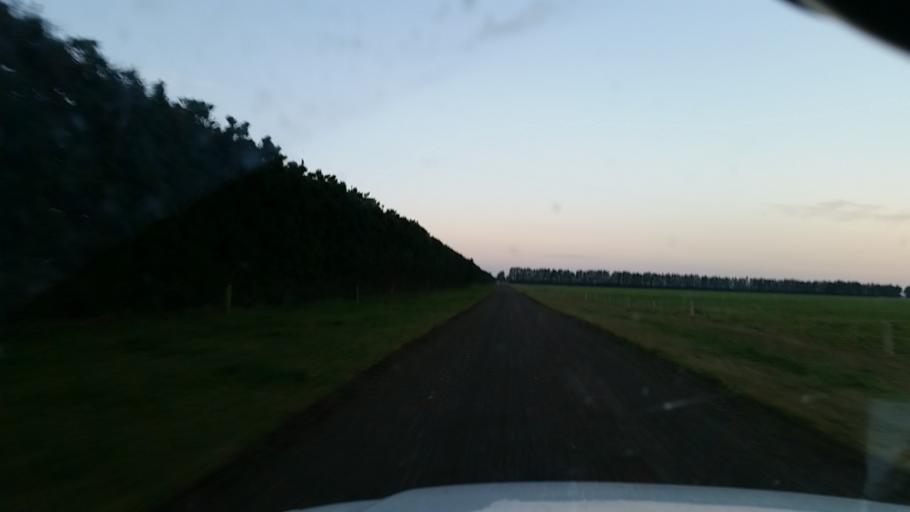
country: NZ
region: Canterbury
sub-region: Ashburton District
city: Tinwald
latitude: -43.9476
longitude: 171.6006
